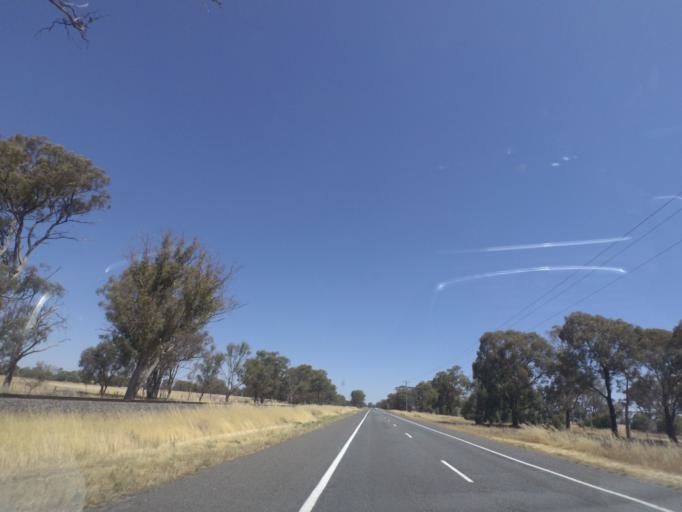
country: AU
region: Victoria
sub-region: Greater Shepparton
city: Shepparton
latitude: -36.2149
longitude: 145.4318
